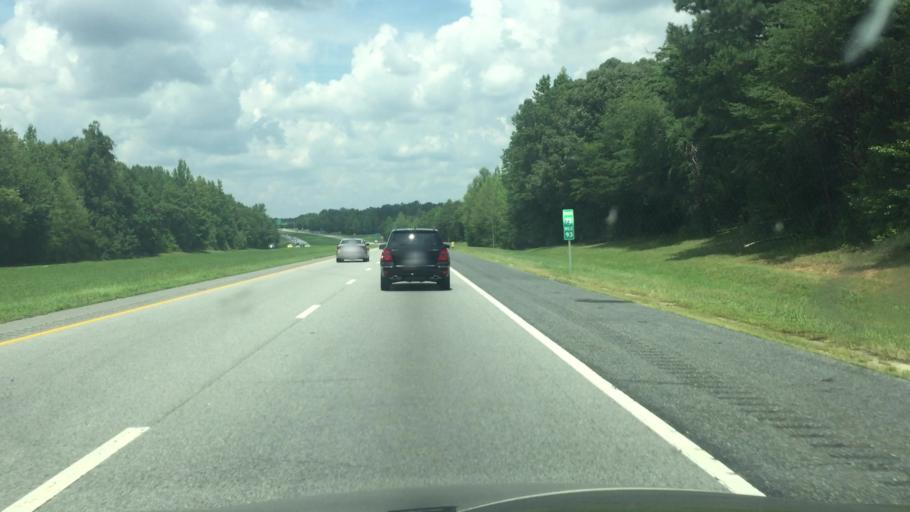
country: US
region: North Carolina
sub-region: Guilford County
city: Pleasant Garden
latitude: 35.9715
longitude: -79.8210
